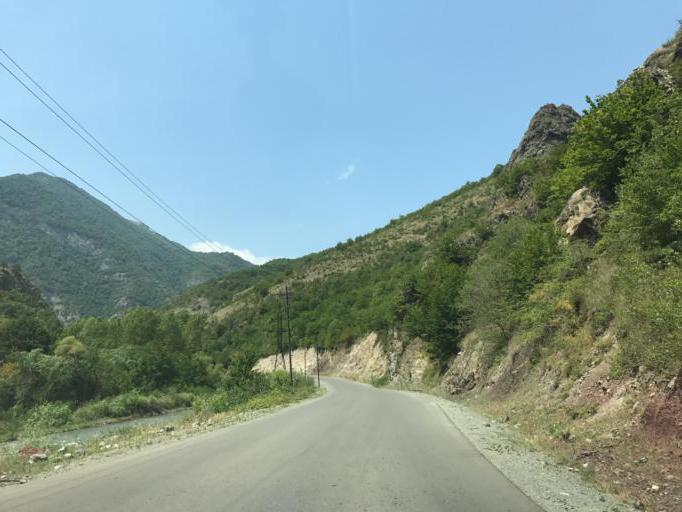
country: AZ
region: Kalbacar Rayonu
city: Kerbakhiar
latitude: 40.1444
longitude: 46.3052
